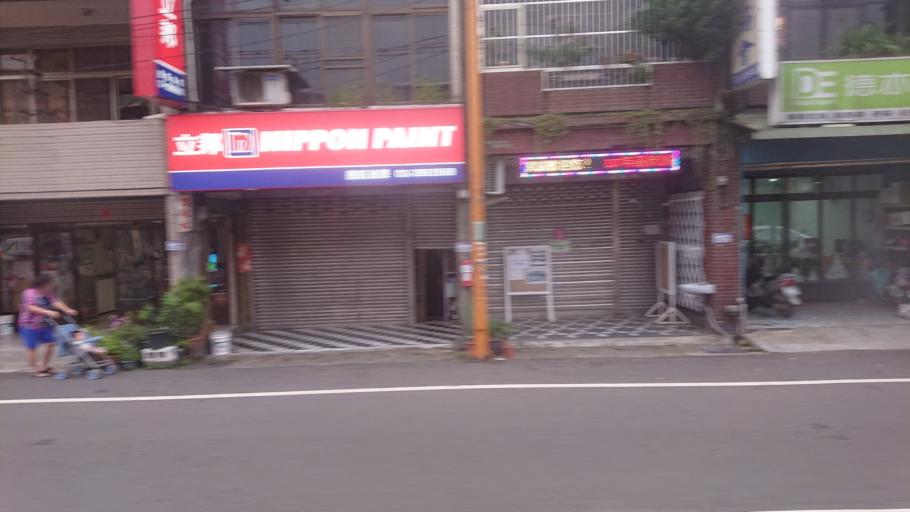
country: TW
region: Taiwan
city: Daxi
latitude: 24.8833
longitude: 121.2669
